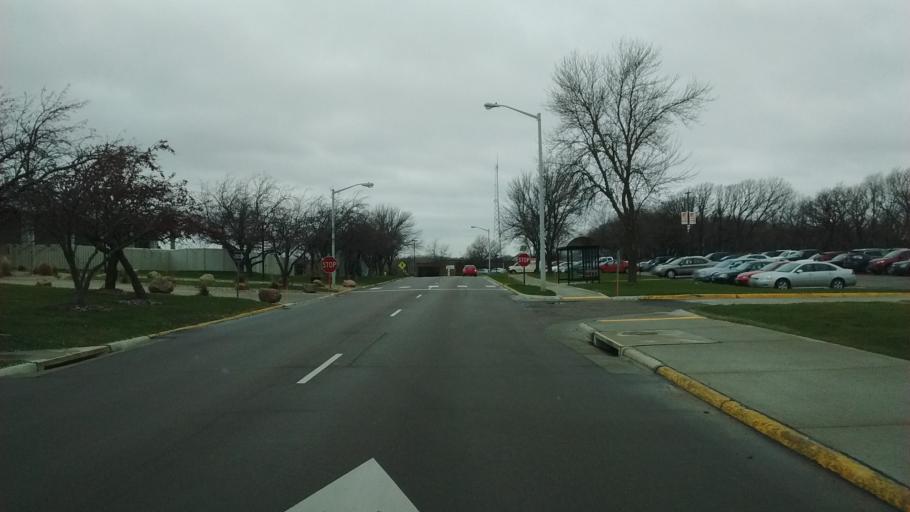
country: US
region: Iowa
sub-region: Woodbury County
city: Sioux City
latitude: 42.4846
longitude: -96.3490
